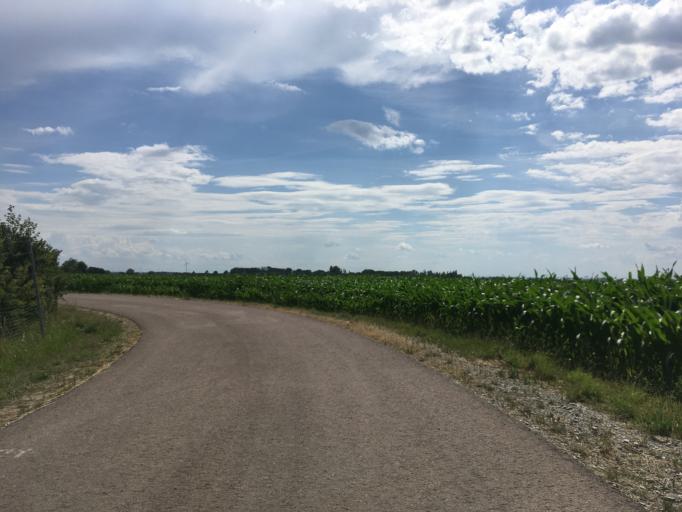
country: DE
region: Saxony-Anhalt
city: Koethen
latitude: 51.7589
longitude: 11.9148
